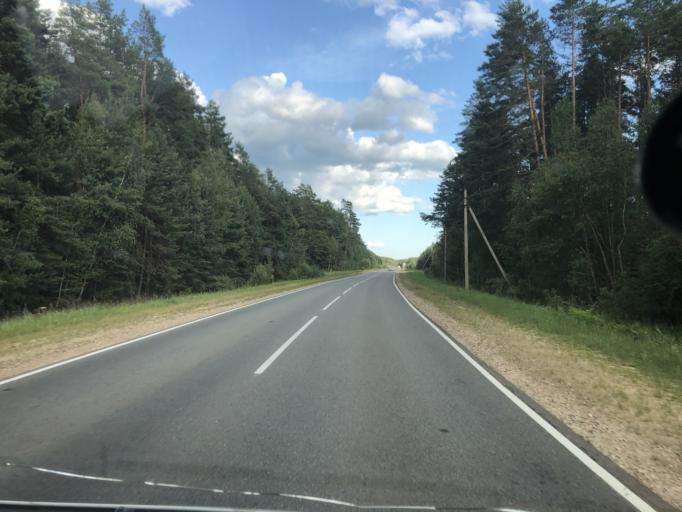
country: RU
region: Kaluga
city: Yukhnov
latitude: 54.7226
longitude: 35.2173
